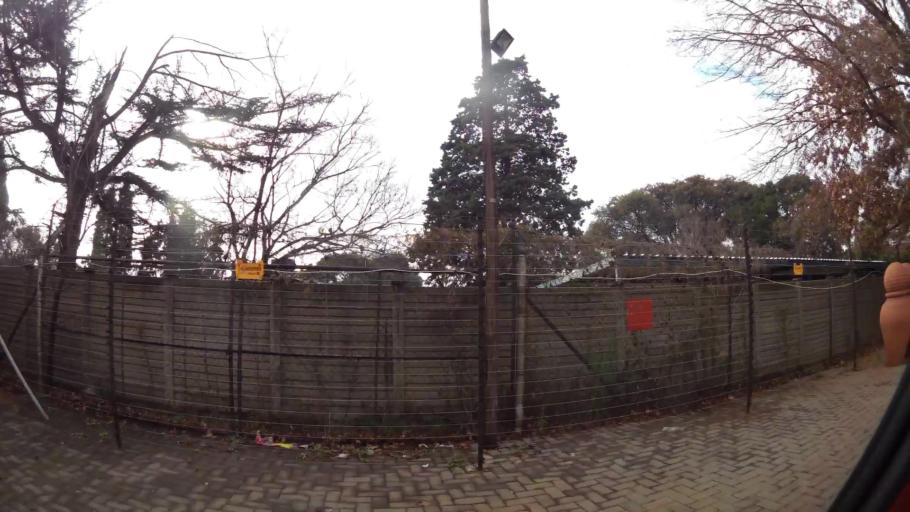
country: ZA
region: Gauteng
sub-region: Sedibeng District Municipality
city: Vanderbijlpark
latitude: -26.7038
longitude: 27.8309
